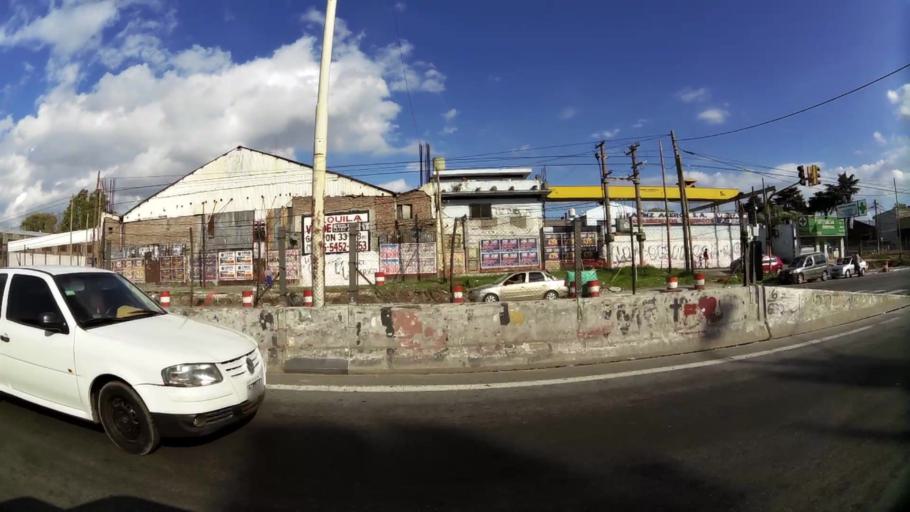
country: AR
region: Buenos Aires
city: San Justo
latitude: -34.6968
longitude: -58.5763
